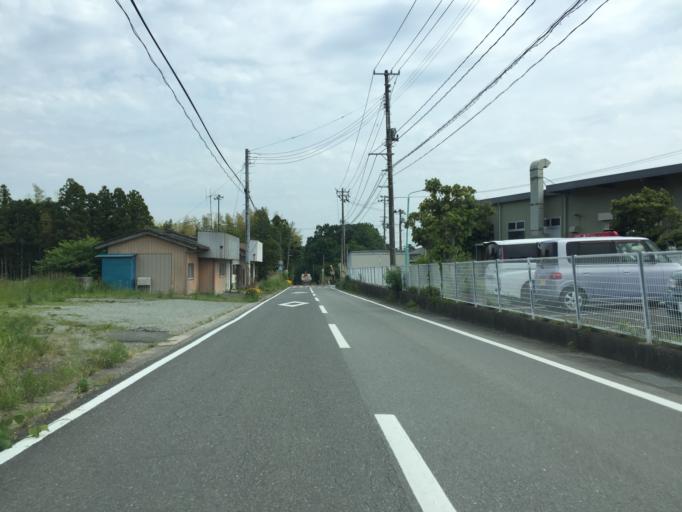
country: JP
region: Fukushima
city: Namie
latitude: 37.2946
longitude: 140.9996
